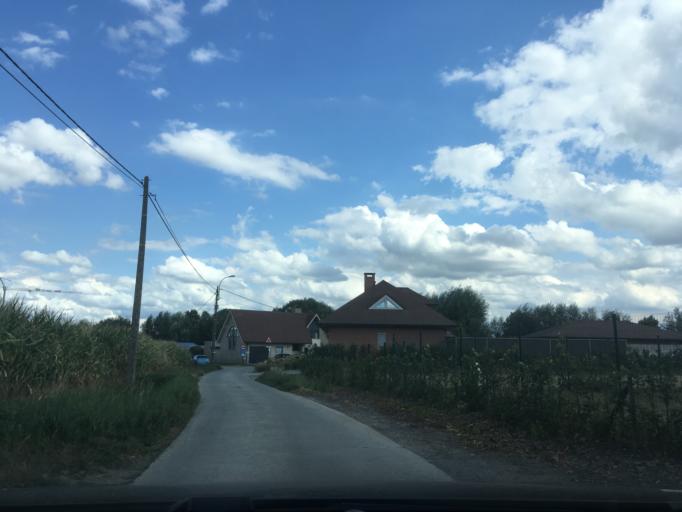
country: BE
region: Flanders
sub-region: Provincie West-Vlaanderen
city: Staden
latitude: 50.9476
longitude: 3.0486
